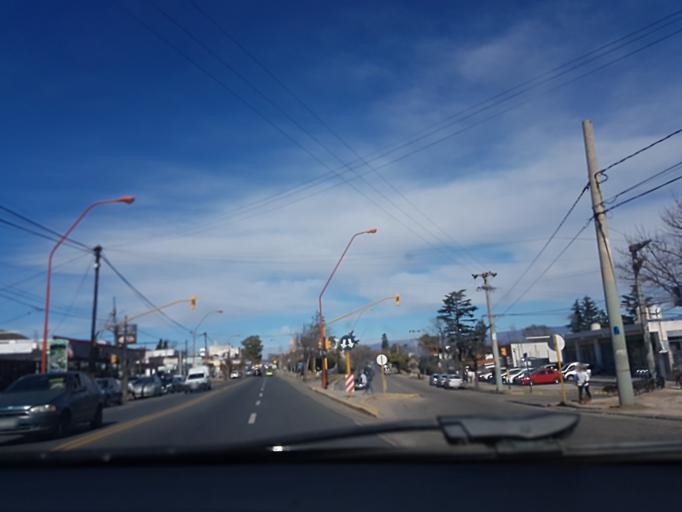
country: AR
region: Cordoba
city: Villa Carlos Paz
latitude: -31.4331
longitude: -64.4988
